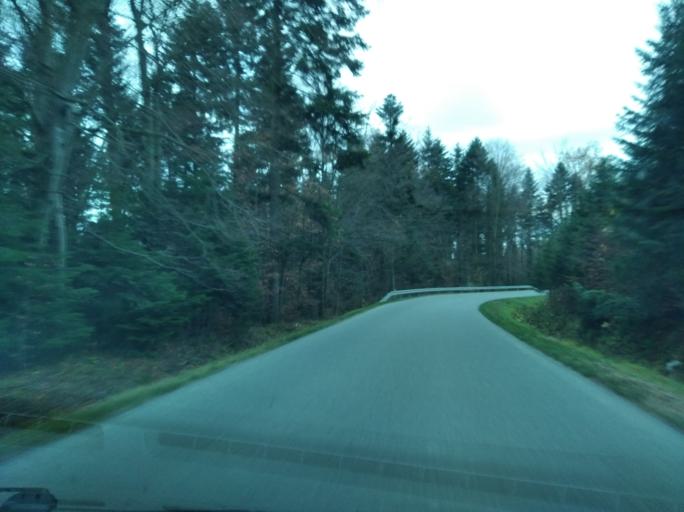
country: PL
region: Subcarpathian Voivodeship
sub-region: Powiat ropczycko-sedziszowski
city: Zagorzyce
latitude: 49.9615
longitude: 21.6919
